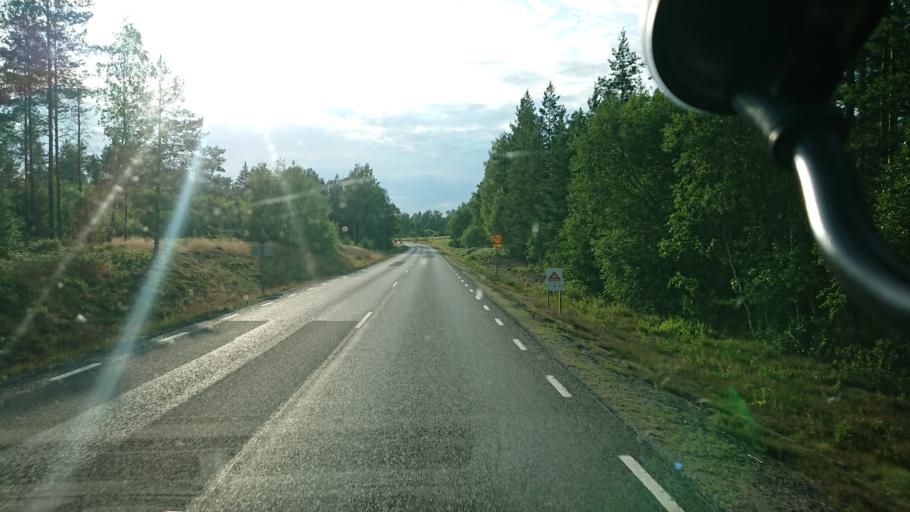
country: SE
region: Kronoberg
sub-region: Vaxjo Kommun
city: Rottne
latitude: 57.0338
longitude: 14.9481
